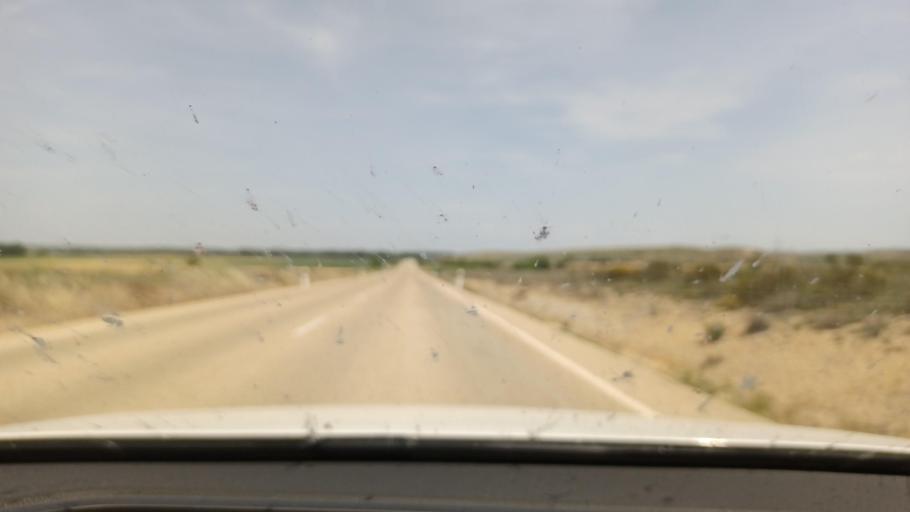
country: ES
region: Castille and Leon
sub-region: Provincia de Soria
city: Velamazan
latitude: 41.4748
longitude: -2.7014
